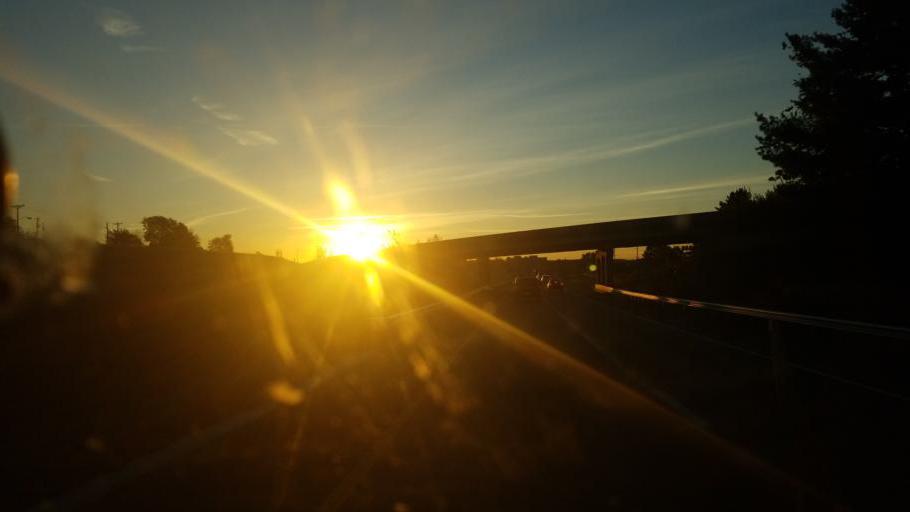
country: US
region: Missouri
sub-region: Boone County
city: Columbia
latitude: 38.9653
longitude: -92.3032
